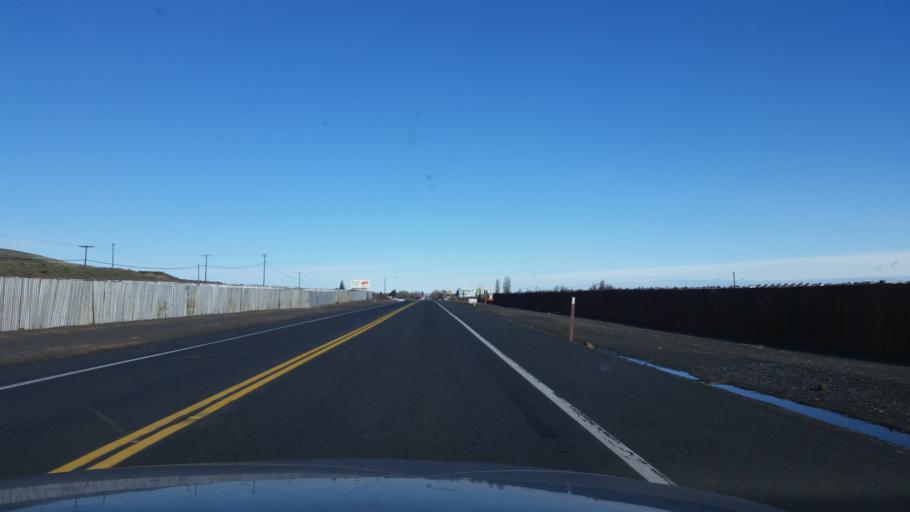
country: US
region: Washington
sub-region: Grant County
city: Ephrata
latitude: 47.2975
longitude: -119.5684
